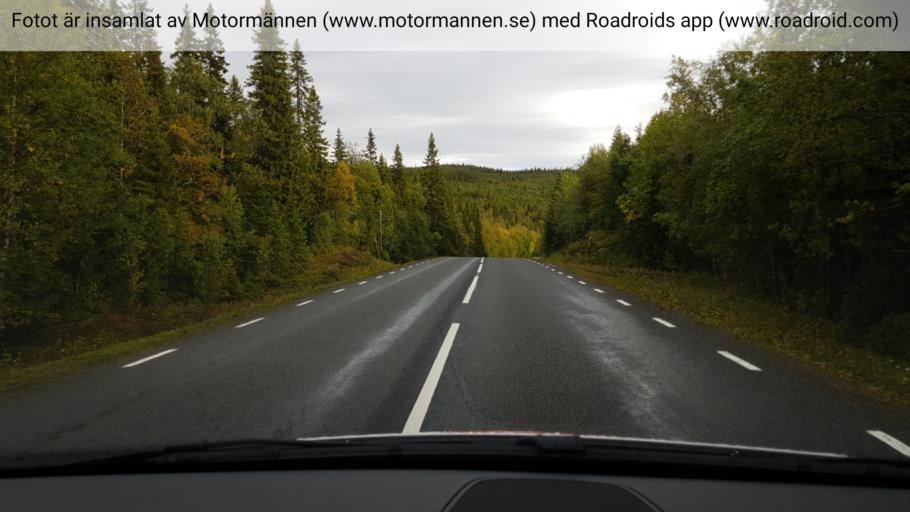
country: SE
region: Jaemtland
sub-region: Are Kommun
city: Are
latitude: 63.4961
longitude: 13.1752
